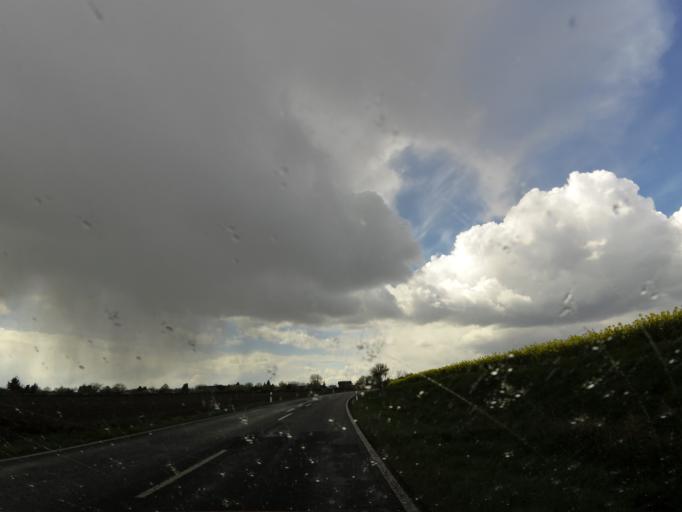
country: DE
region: Saxony-Anhalt
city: Wanzleben
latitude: 52.0665
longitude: 11.4537
